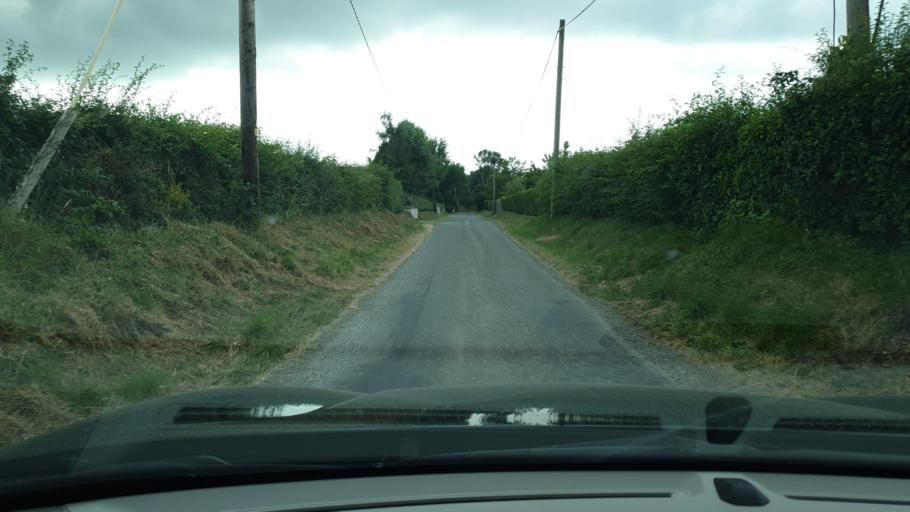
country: IE
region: Leinster
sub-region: An Mhi
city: Ratoath
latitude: 53.4695
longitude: -6.4597
